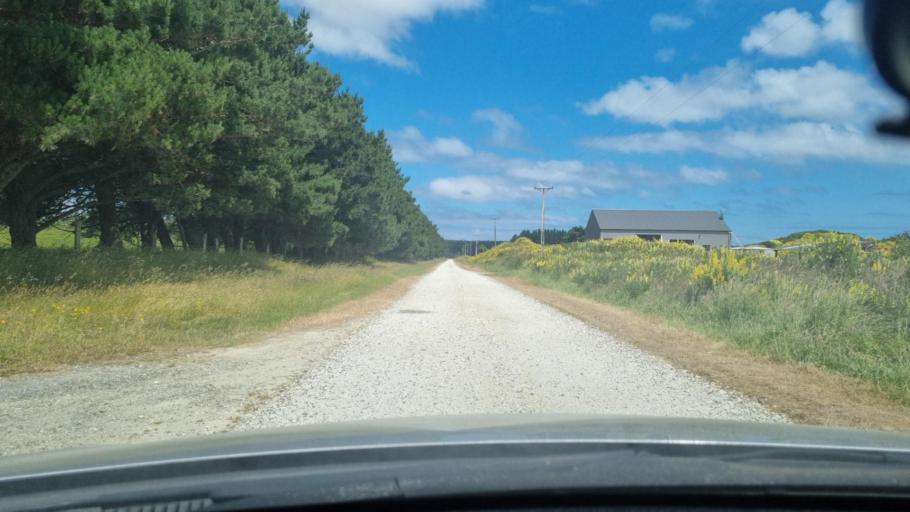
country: NZ
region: Southland
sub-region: Invercargill City
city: Invercargill
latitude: -46.4547
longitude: 168.2755
